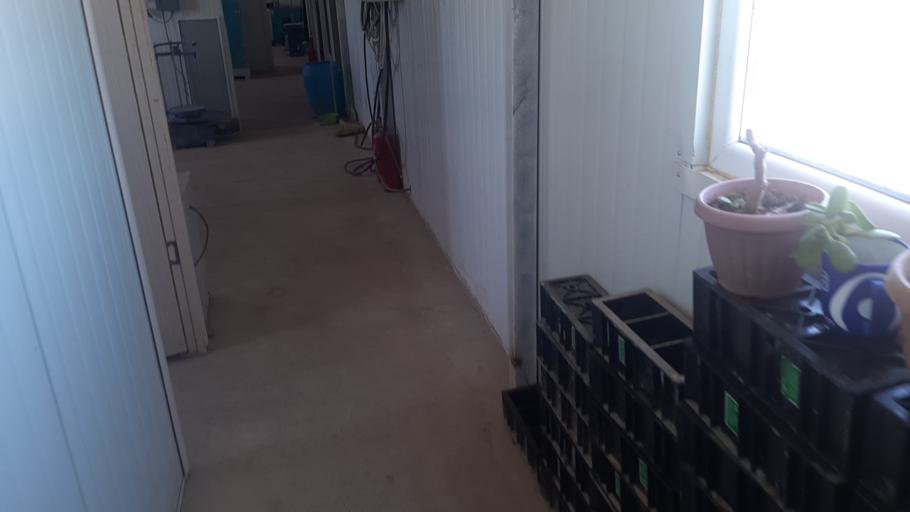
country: KZ
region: Qaraghandy
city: Balqash
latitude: 46.6459
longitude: 74.3972
